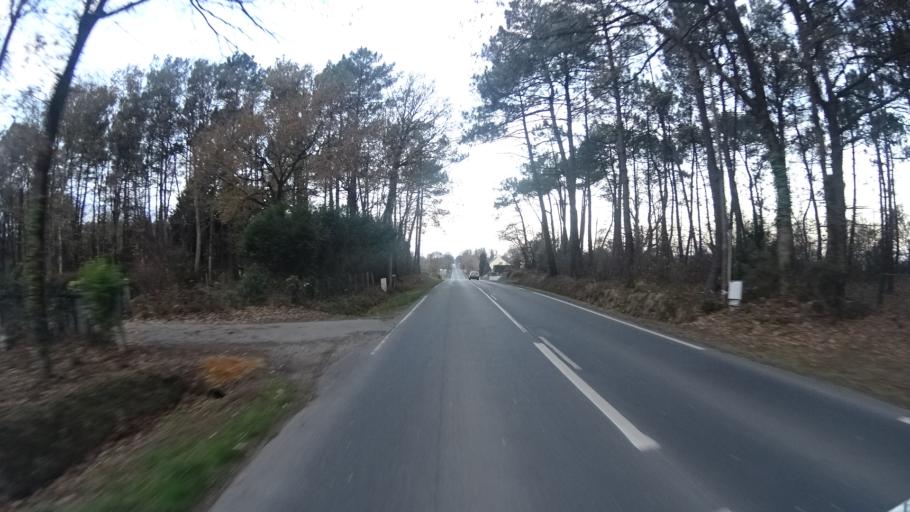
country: FR
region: Pays de la Loire
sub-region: Departement de la Loire-Atlantique
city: Avessac
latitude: 47.6406
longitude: -2.0162
